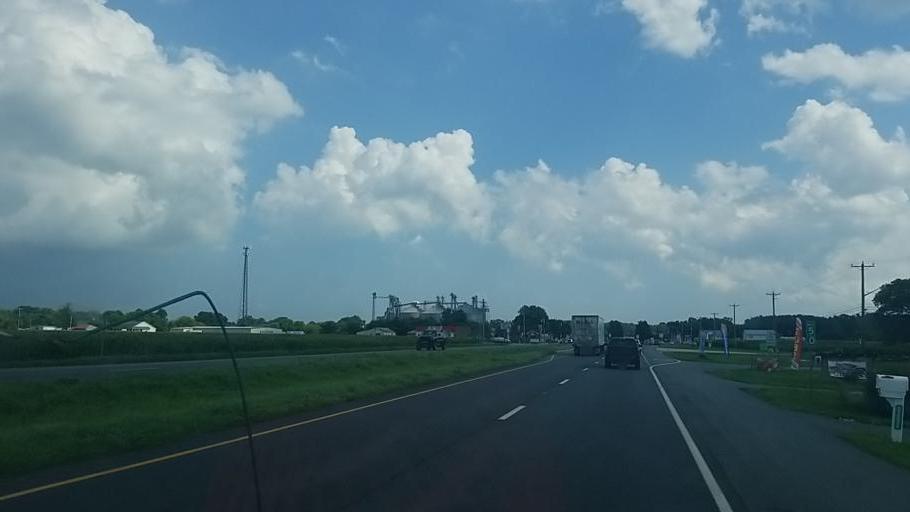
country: US
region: Delaware
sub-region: Sussex County
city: Selbyville
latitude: 38.5223
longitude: -75.2436
